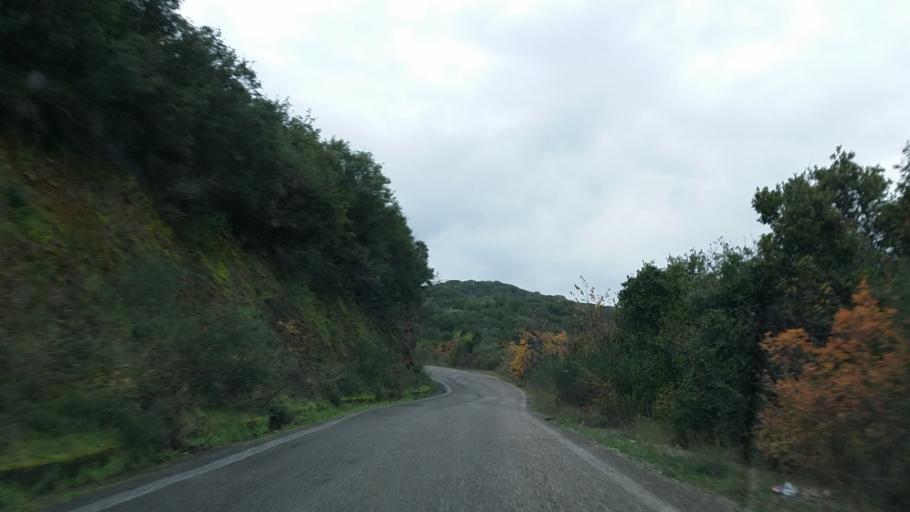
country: GR
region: West Greece
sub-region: Nomos Aitolias kai Akarnanias
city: Fitiai
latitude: 38.7204
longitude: 21.1864
